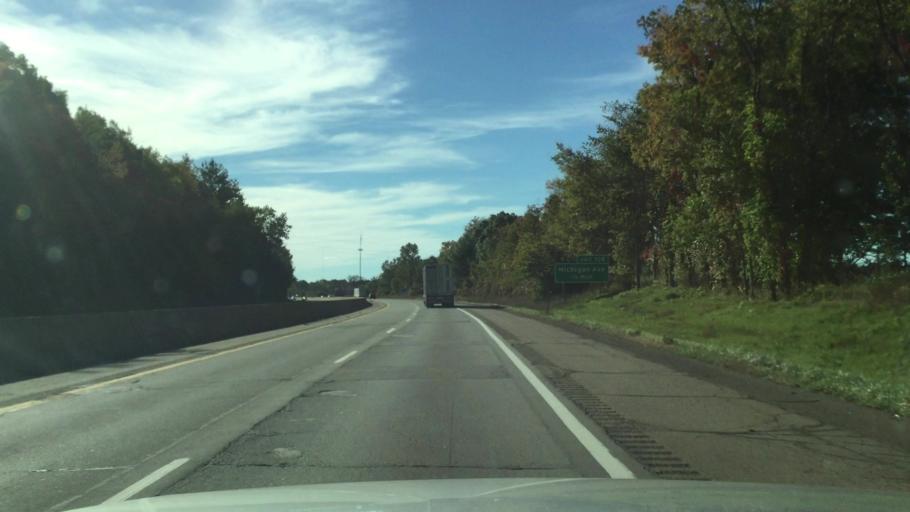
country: US
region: Michigan
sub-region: Jackson County
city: Spring Arbor
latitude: 42.2692
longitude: -84.6070
